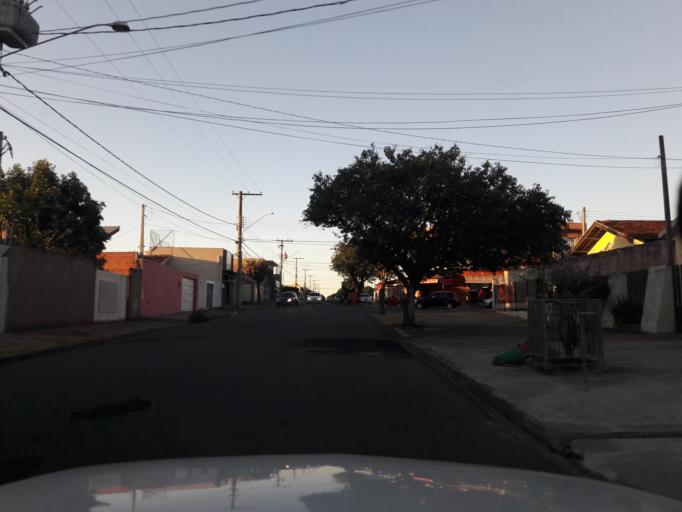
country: BR
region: Sao Paulo
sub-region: Moji-Guacu
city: Mogi-Gaucu
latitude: -22.3517
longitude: -46.9354
